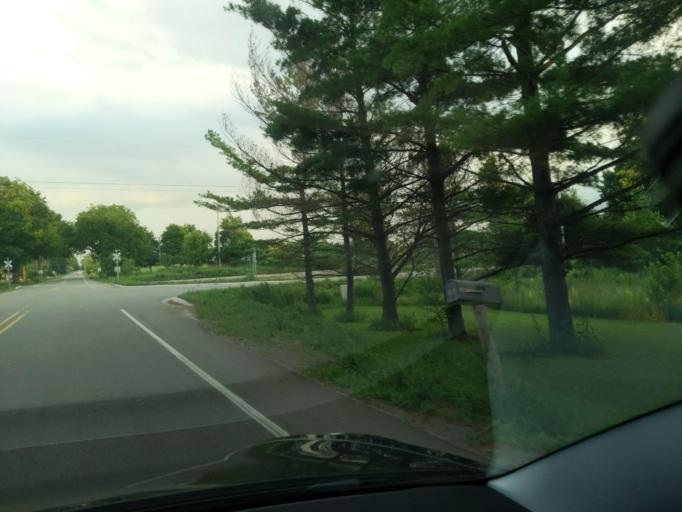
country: US
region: Michigan
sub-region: Ingham County
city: Mason
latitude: 42.5240
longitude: -84.4287
